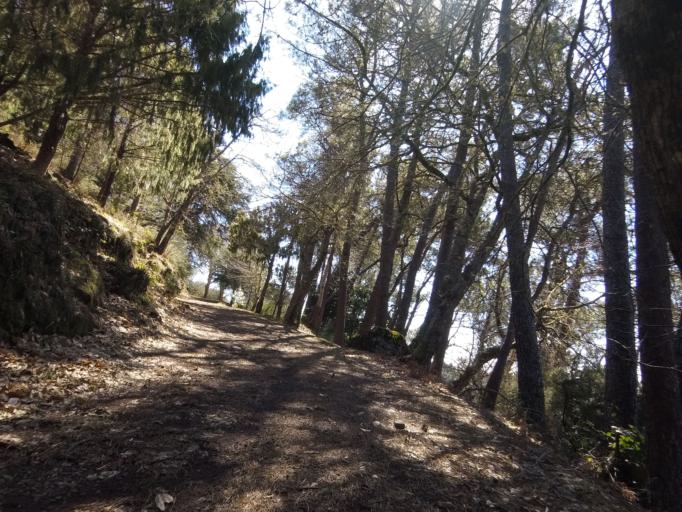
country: PT
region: Madeira
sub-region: Funchal
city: Nossa Senhora do Monte
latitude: 32.7049
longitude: -16.8868
